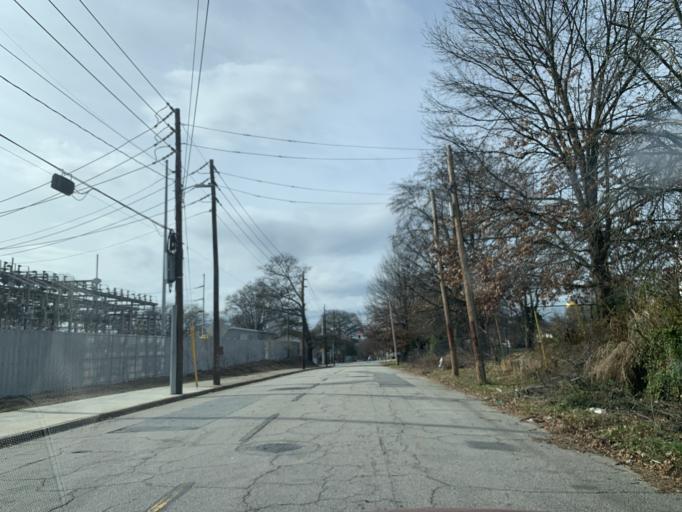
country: US
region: Georgia
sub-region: Fulton County
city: Atlanta
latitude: 33.7457
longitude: -84.3778
